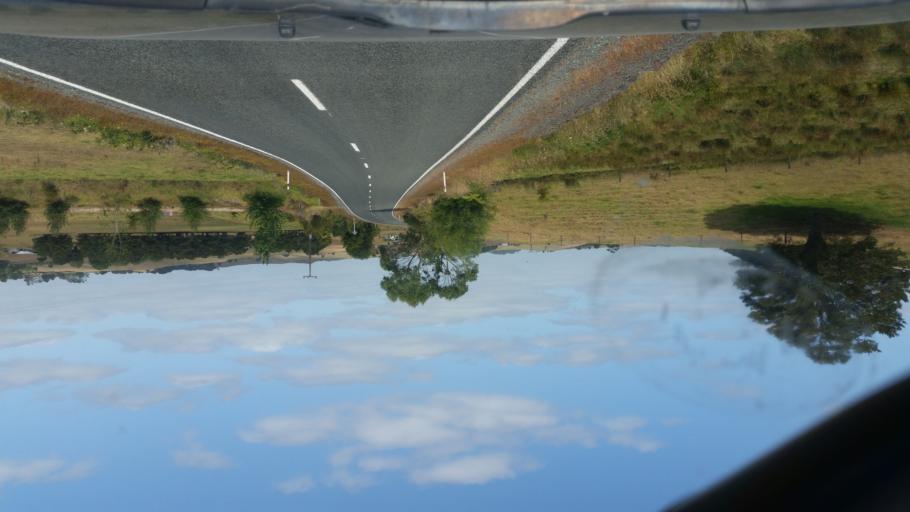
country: NZ
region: Northland
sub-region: Whangarei
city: Ruakaka
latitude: -35.9594
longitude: 174.2923
